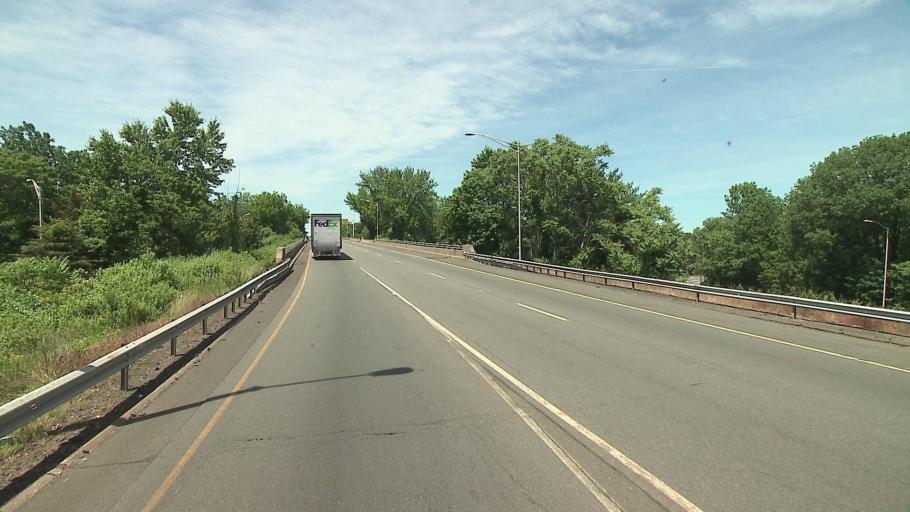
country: US
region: Connecticut
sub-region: New Haven County
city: Meriden
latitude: 41.5398
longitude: -72.7698
